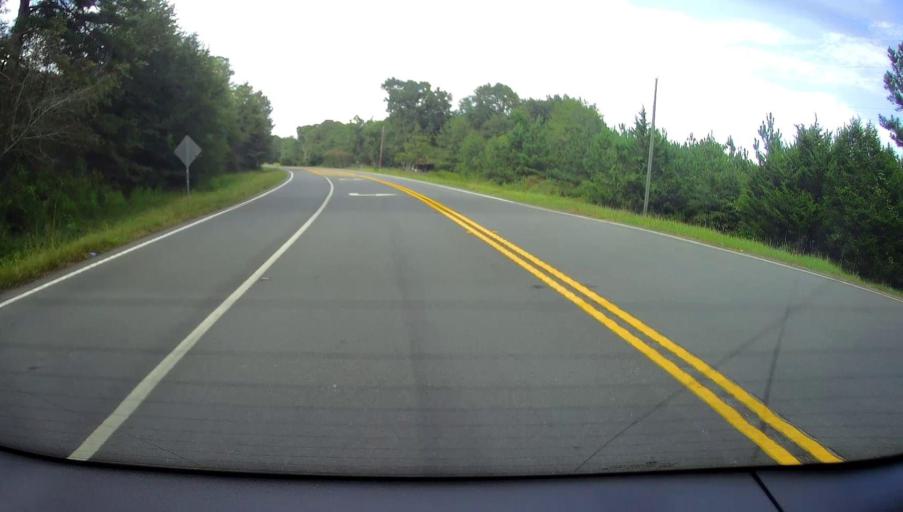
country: US
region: Georgia
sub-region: Meriwether County
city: Manchester
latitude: 32.9654
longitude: -84.6021
